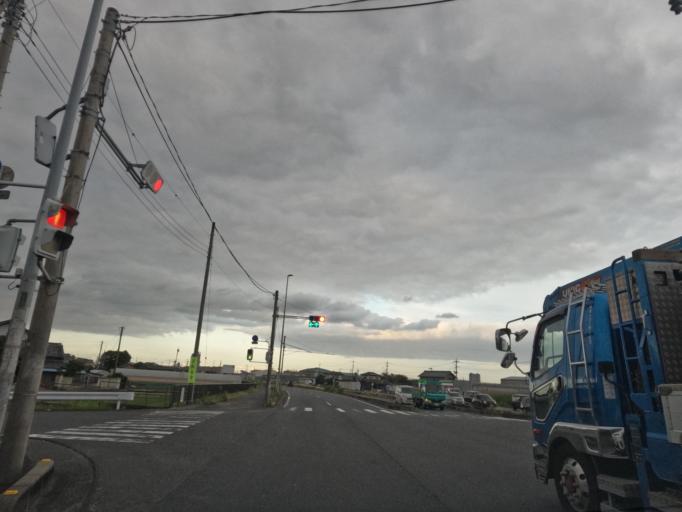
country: JP
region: Saitama
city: Koshigaya
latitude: 35.8975
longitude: 139.7588
